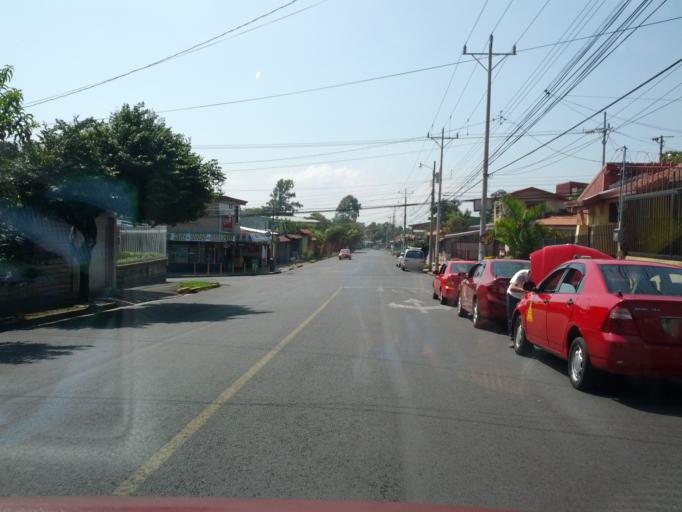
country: CR
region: Alajuela
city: Alajuela
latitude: 10.0146
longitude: -84.2024
